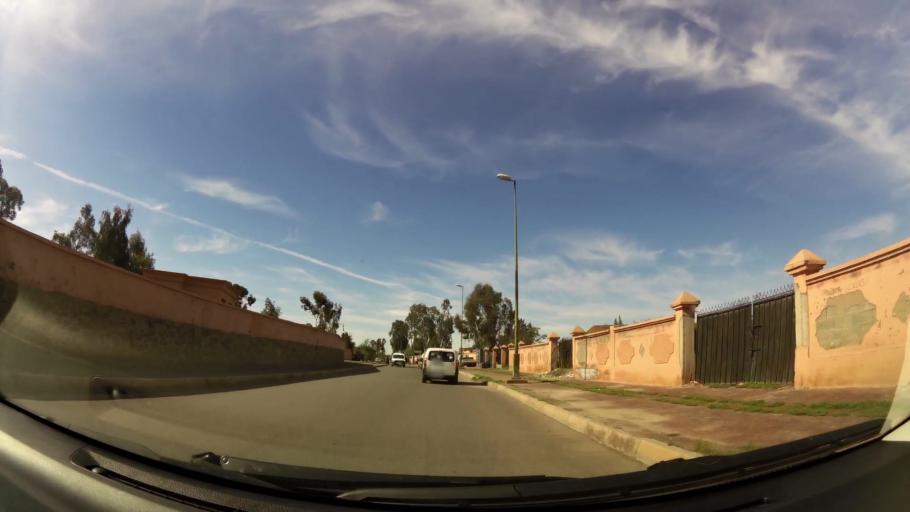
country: MA
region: Marrakech-Tensift-Al Haouz
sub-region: Marrakech
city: Marrakesh
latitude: 31.6073
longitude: -7.9570
